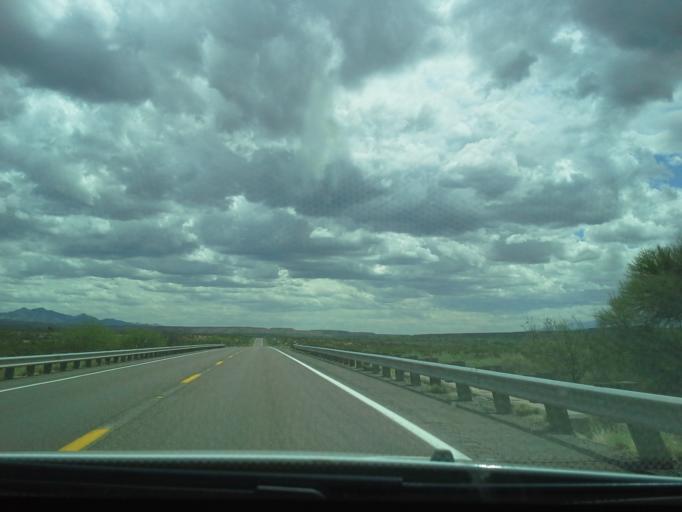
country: US
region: Arizona
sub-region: Graham County
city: Bylas
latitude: 33.1914
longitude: -110.1717
